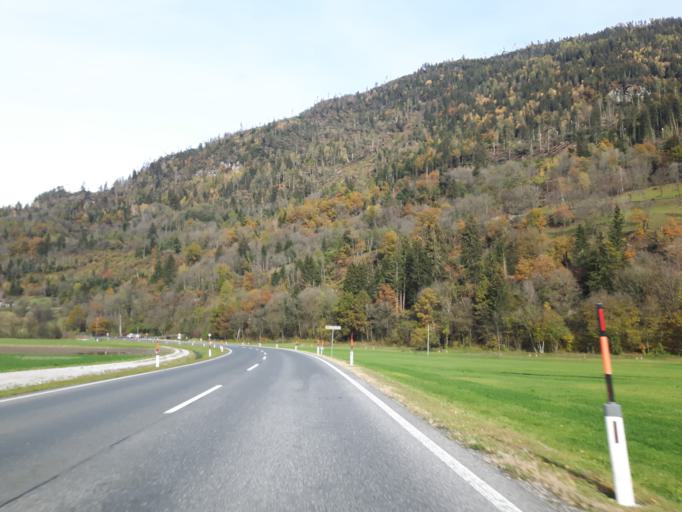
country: AT
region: Tyrol
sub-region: Politischer Bezirk Lienz
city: Lavant
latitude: 46.7997
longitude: 12.8736
